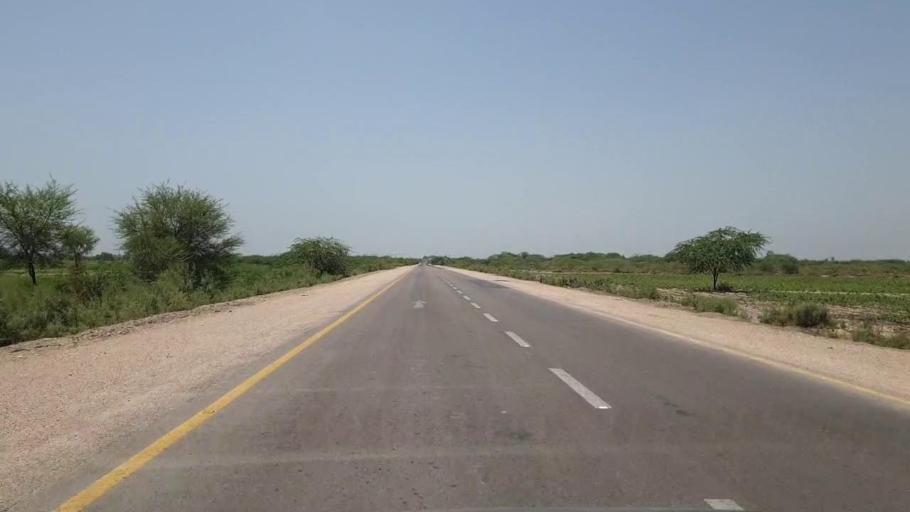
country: PK
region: Sindh
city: Sakrand
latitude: 26.1188
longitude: 68.3851
